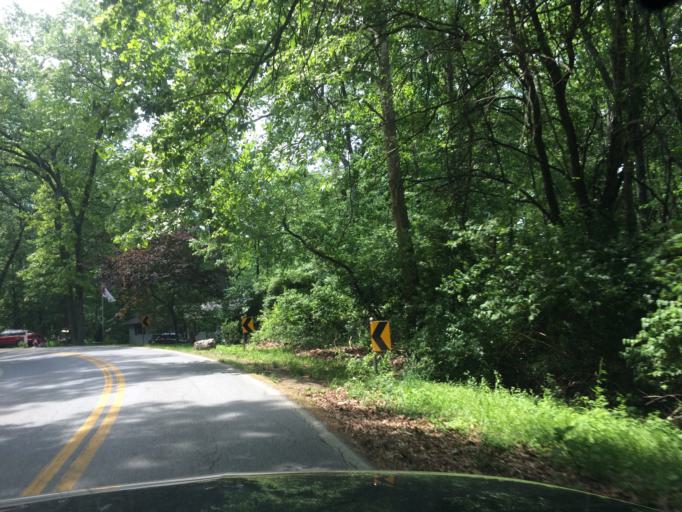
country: US
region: Maryland
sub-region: Carroll County
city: Sykesville
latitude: 39.3977
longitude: -76.9925
